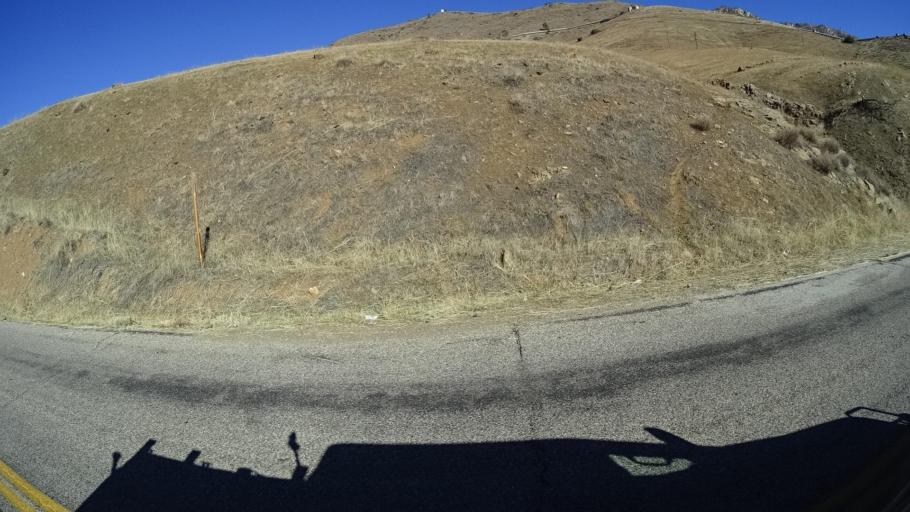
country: US
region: California
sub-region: Kern County
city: Kernville
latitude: 35.7788
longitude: -118.4377
